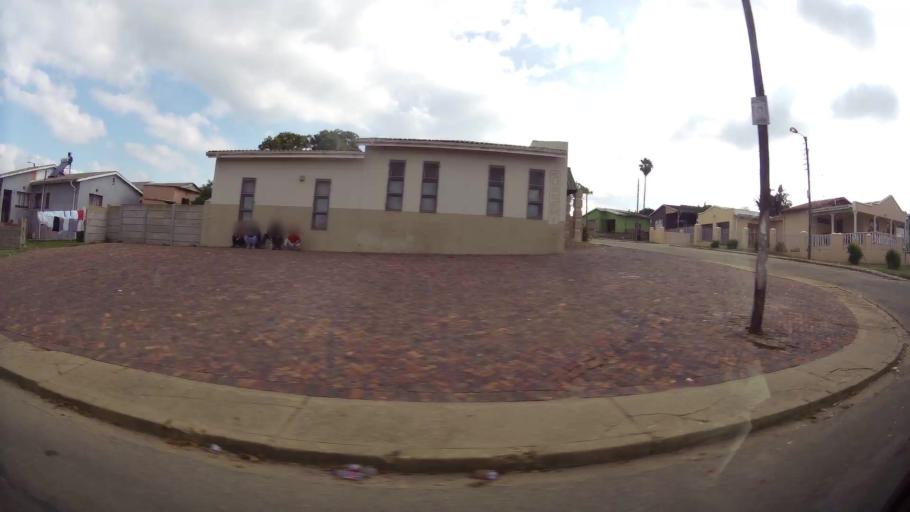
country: ZA
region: Eastern Cape
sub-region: Nelson Mandela Bay Metropolitan Municipality
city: Uitenhage
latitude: -33.7367
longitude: 25.3812
